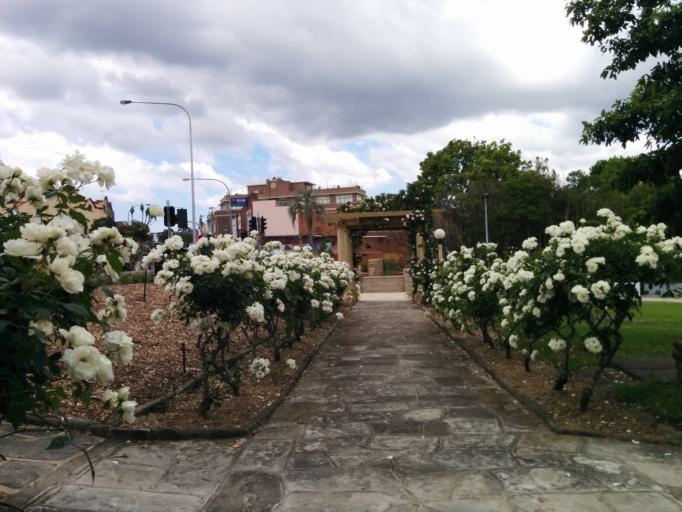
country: AU
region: New South Wales
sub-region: Hornsby Shire
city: Hornsby
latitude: -33.7016
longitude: 151.0966
